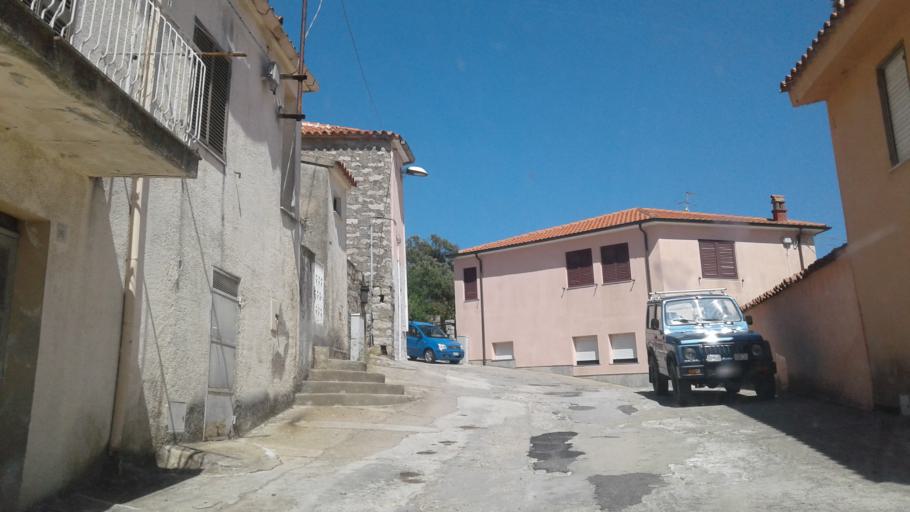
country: IT
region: Sardinia
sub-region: Provincia di Olbia-Tempio
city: Aggius
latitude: 40.9303
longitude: 9.0678
